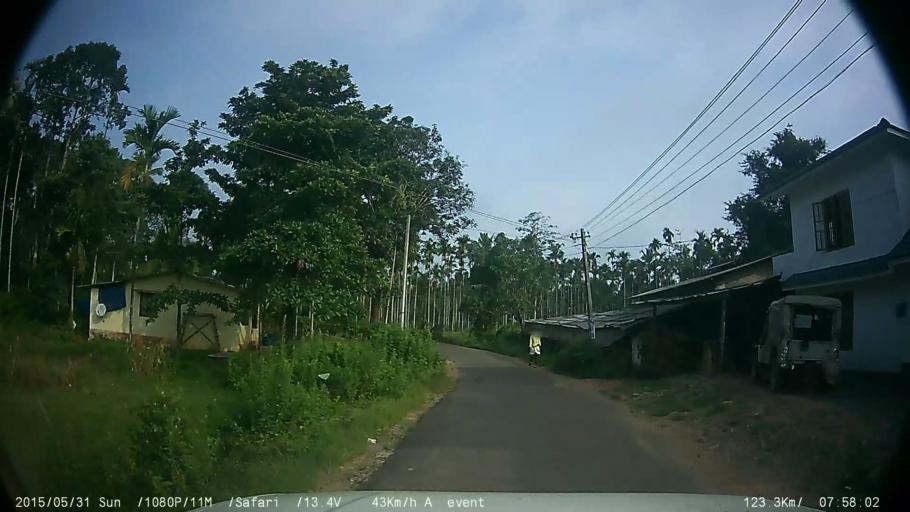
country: IN
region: Kerala
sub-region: Wayanad
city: Kalpetta
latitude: 11.6335
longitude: 76.0633
